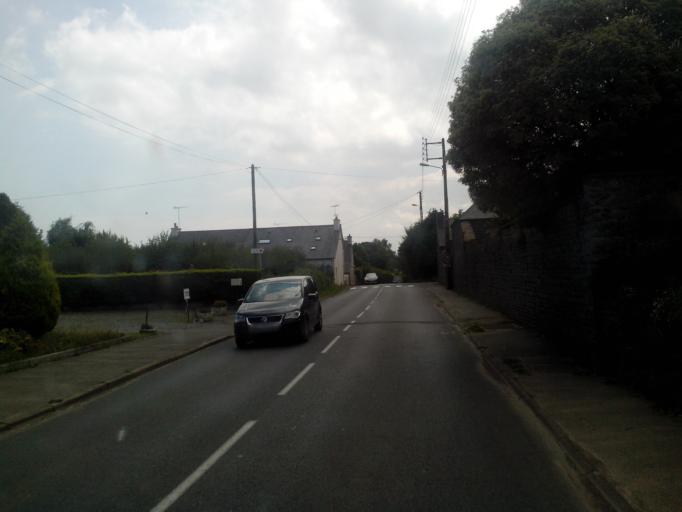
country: FR
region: Brittany
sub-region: Departement des Cotes-d'Armor
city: Plouezec
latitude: 48.7466
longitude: -2.9834
